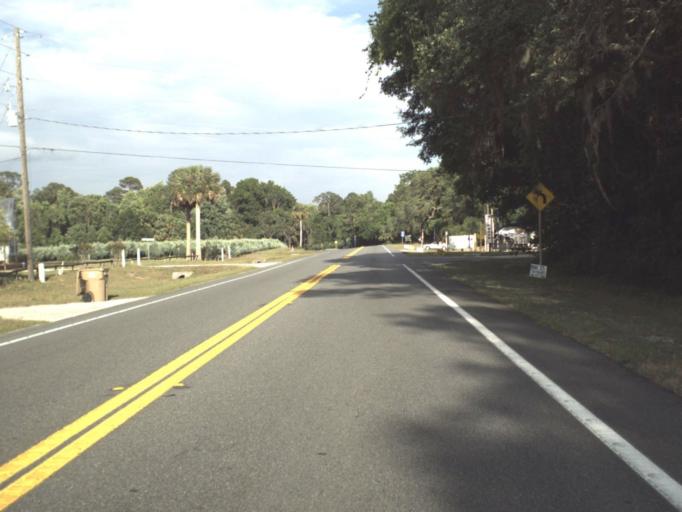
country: US
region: Florida
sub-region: Lake County
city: Astor
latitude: 29.1539
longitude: -81.5730
